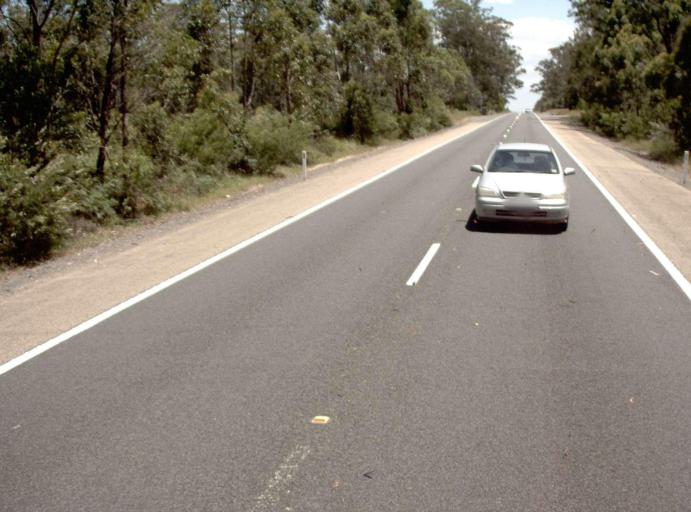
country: AU
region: Victoria
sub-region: East Gippsland
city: Lakes Entrance
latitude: -37.7536
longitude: 148.3261
